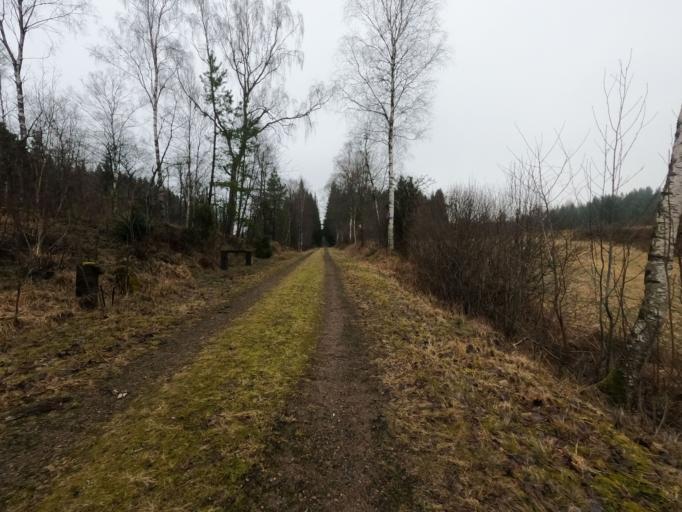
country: SE
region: Halland
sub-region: Hylte Kommun
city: Hyltebruk
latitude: 56.8008
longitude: 13.2538
